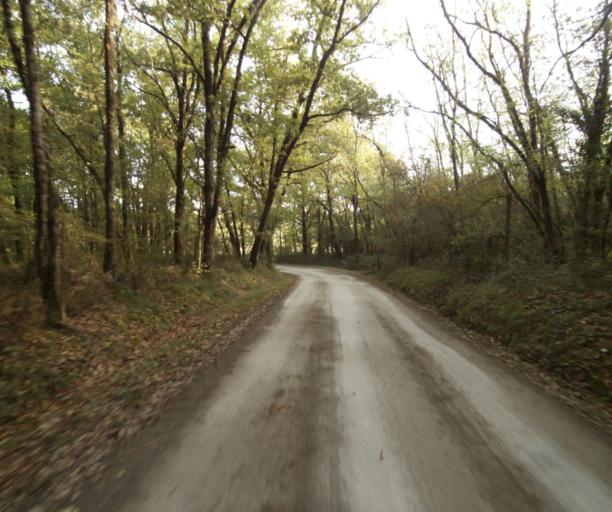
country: FR
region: Midi-Pyrenees
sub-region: Departement de la Haute-Garonne
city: Villemur-sur-Tarn
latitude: 43.9214
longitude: 1.5060
